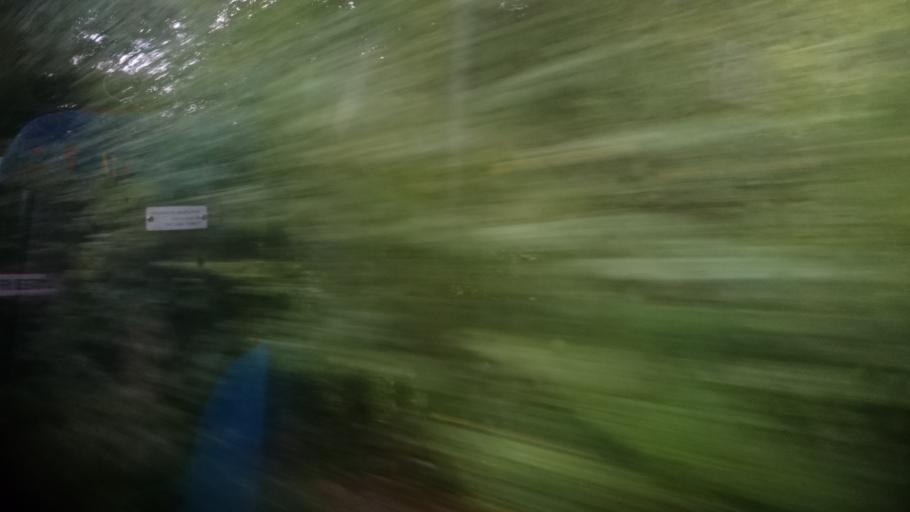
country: ES
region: Asturias
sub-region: Province of Asturias
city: Cangas de Onis
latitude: 43.3217
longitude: -5.0761
